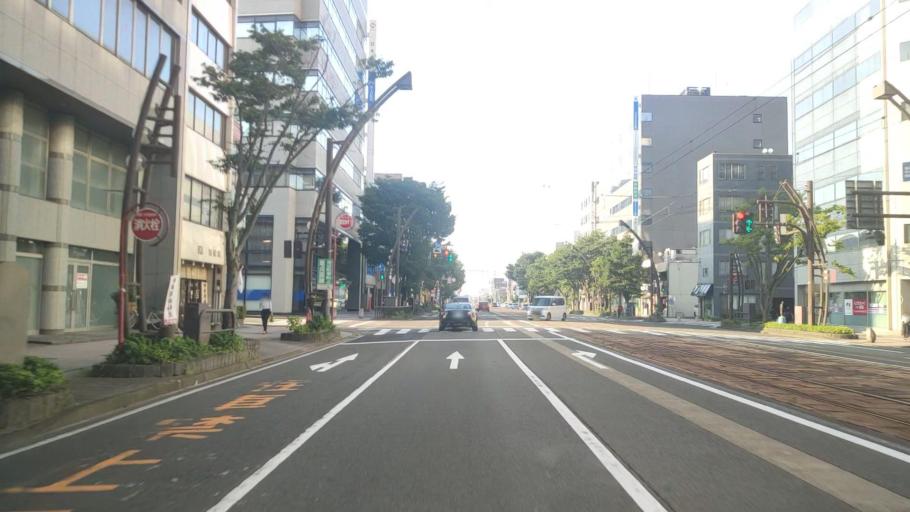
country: JP
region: Fukui
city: Fukui-shi
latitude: 36.0649
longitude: 136.2176
